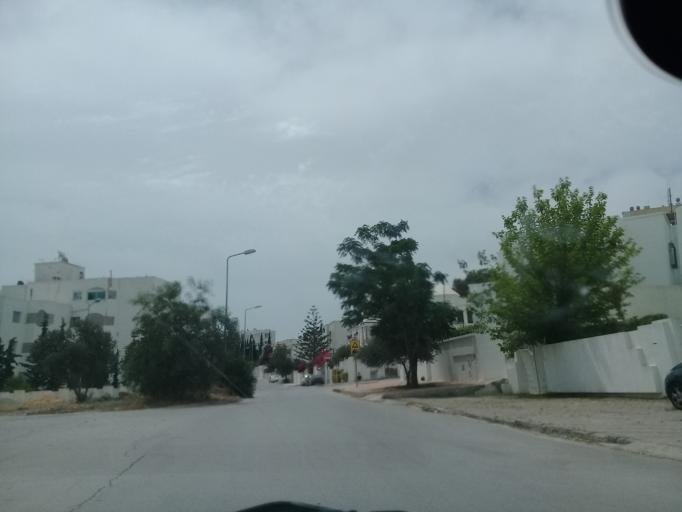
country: TN
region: Tunis
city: Tunis
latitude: 36.8381
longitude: 10.1525
